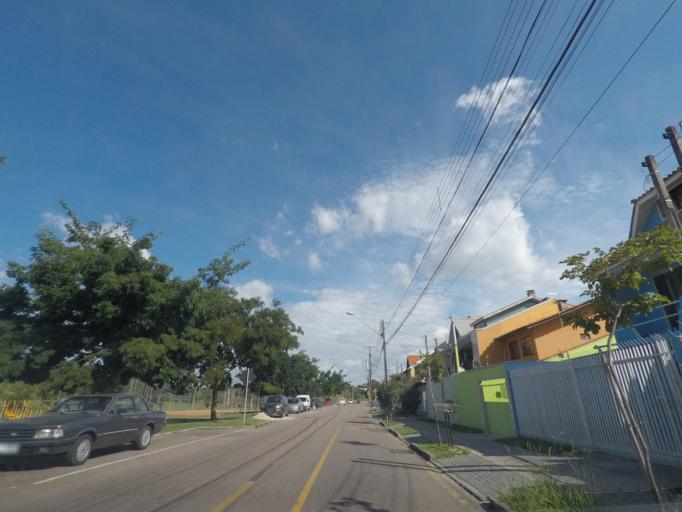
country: BR
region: Parana
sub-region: Curitiba
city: Curitiba
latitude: -25.4791
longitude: -49.3351
